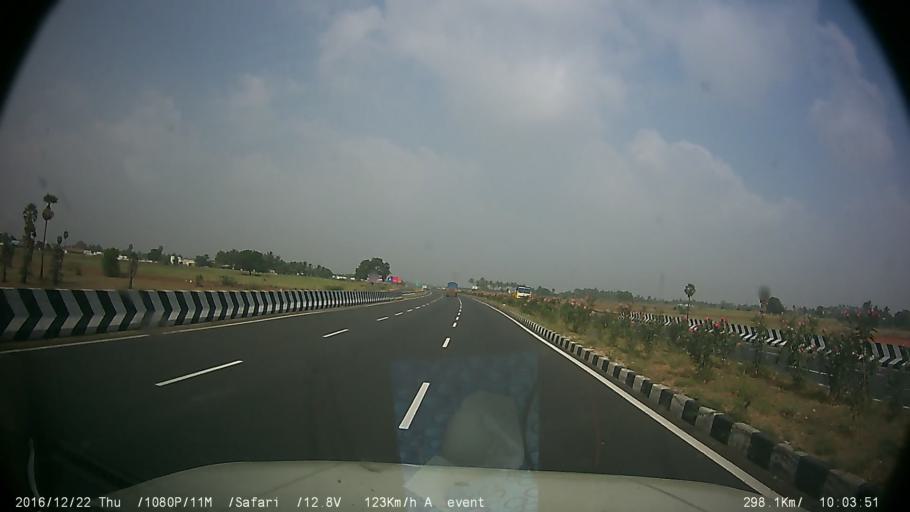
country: IN
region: Tamil Nadu
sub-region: Tiruppur
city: Uttukkuli
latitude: 11.2079
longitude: 77.3721
